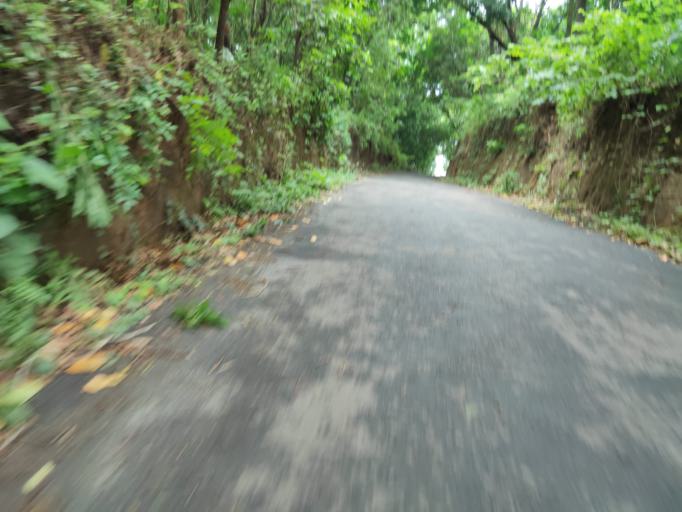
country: IN
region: Kerala
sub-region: Malappuram
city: Manjeri
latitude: 11.2340
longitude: 76.2501
